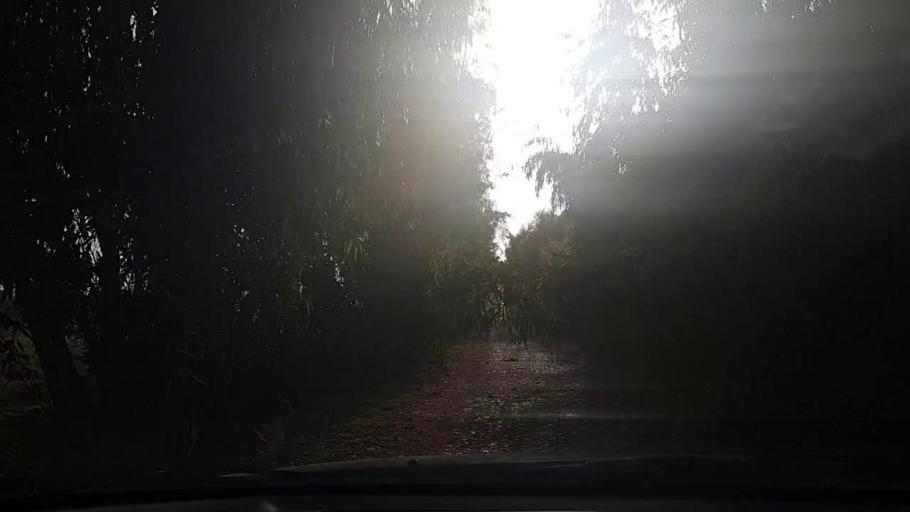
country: PK
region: Sindh
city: Keti Bandar
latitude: 24.2749
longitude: 67.5973
